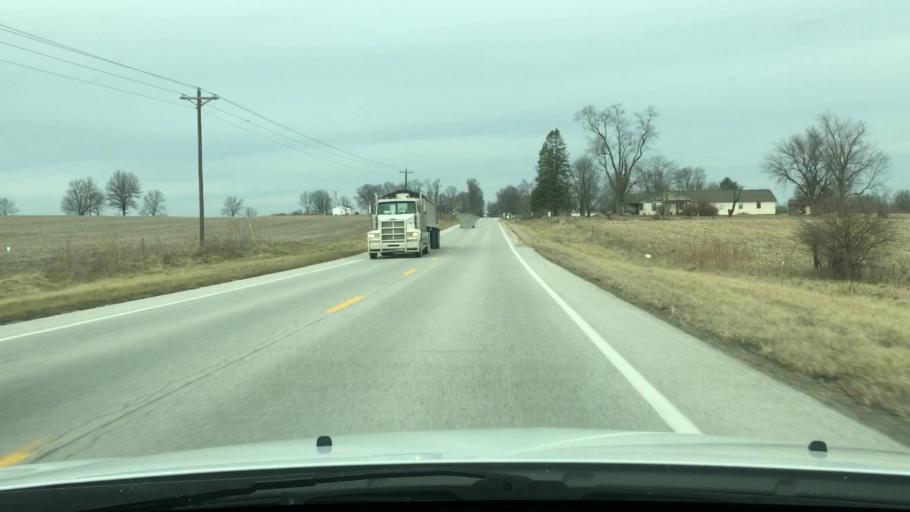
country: US
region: Illinois
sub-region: Pike County
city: Pittsfield
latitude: 39.5385
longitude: -90.9205
